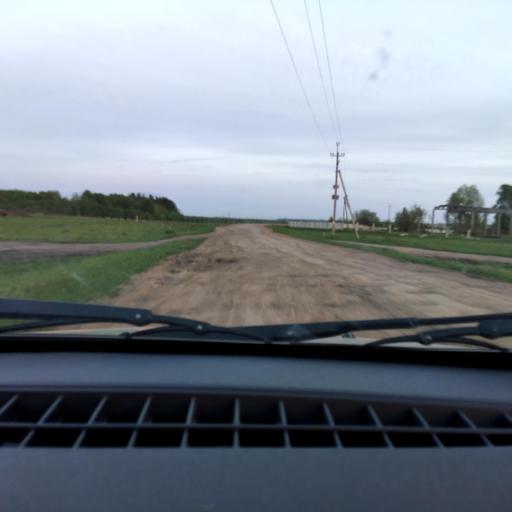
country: RU
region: Bashkortostan
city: Iglino
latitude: 54.9083
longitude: 56.3951
